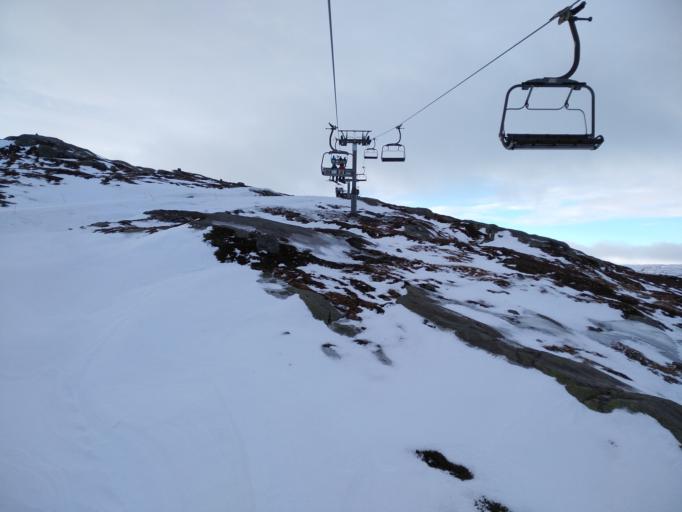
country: NO
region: Vest-Agder
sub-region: Sirdal
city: Tonstad
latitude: 58.9122
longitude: 6.8162
